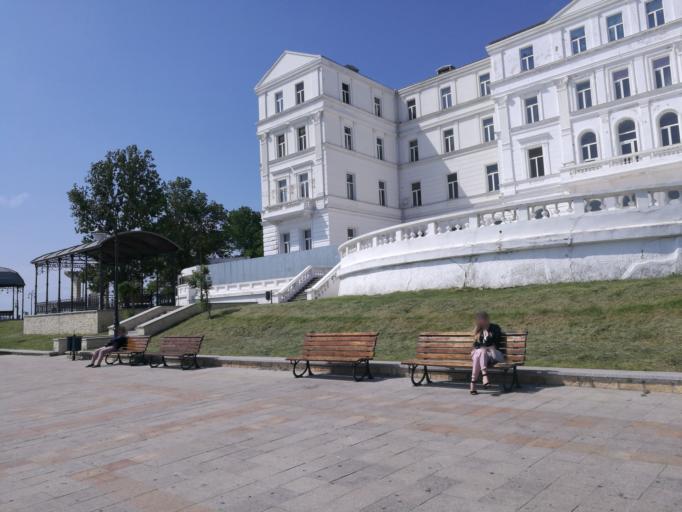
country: RO
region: Constanta
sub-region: Municipiul Constanta
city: Constanta
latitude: 44.1729
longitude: 28.6651
